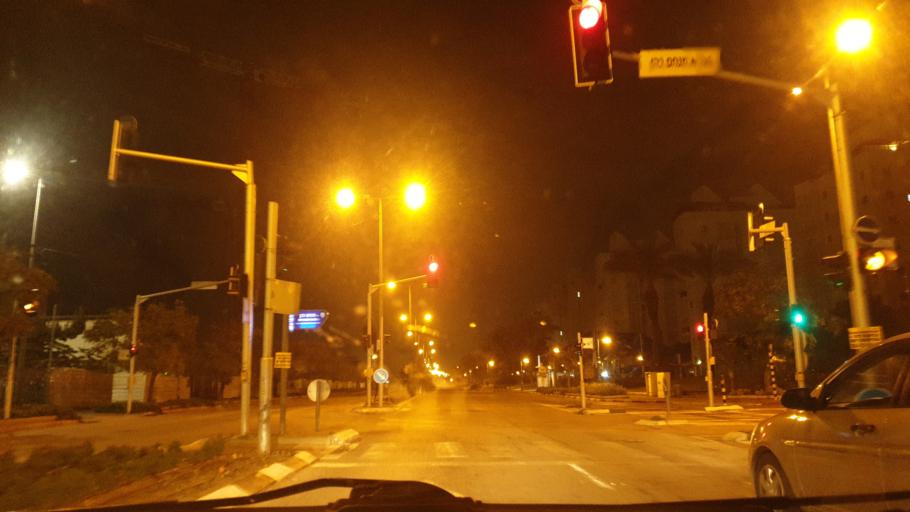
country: IL
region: Central District
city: Bet Dagan
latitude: 31.9753
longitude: 34.8135
